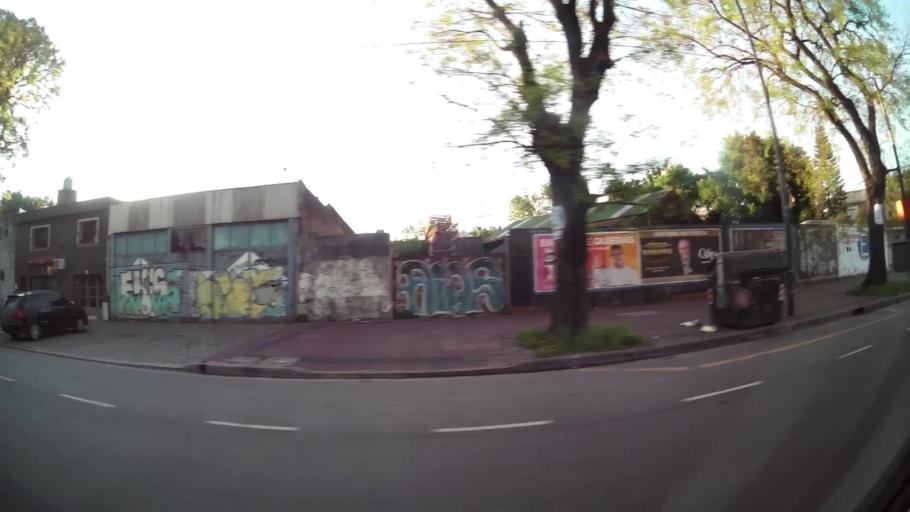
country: AR
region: Buenos Aires F.D.
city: Buenos Aires
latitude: -34.6414
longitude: -58.4126
